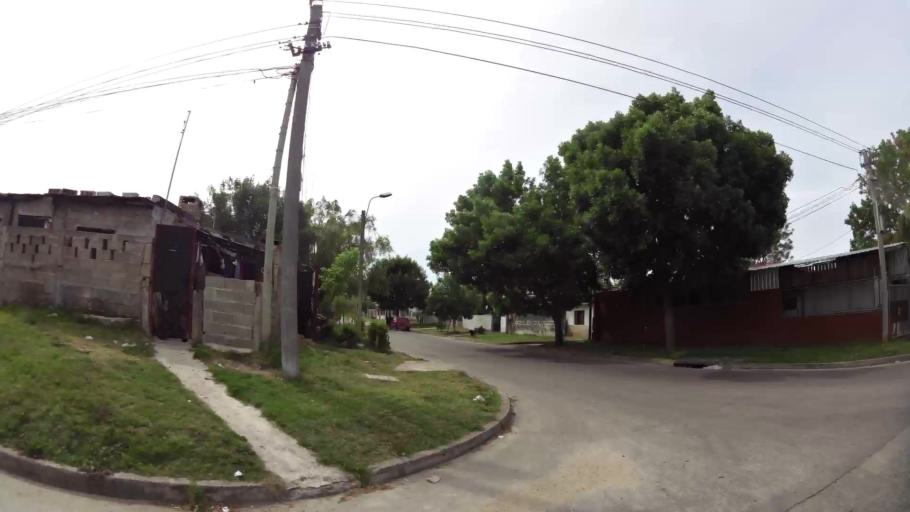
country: UY
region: Montevideo
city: Montevideo
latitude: -34.8415
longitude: -56.1720
